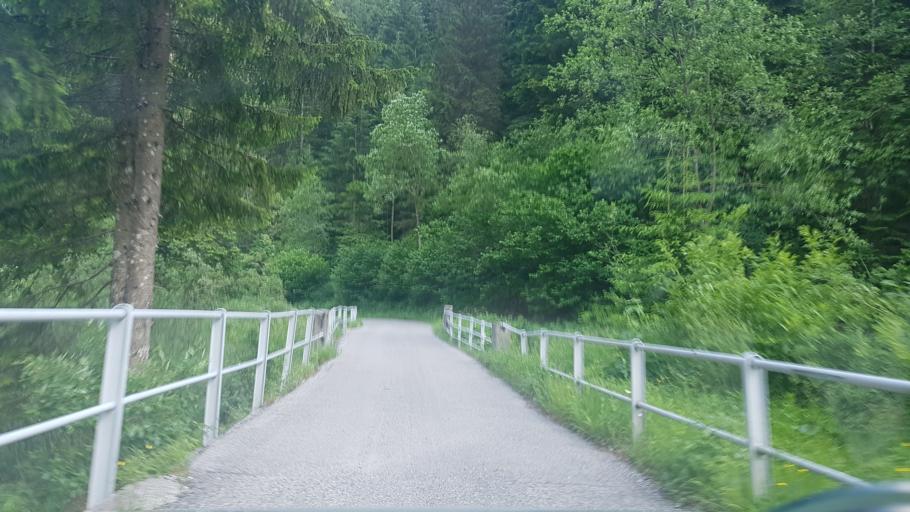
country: IT
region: Friuli Venezia Giulia
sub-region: Provincia di Udine
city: Pontebba
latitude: 46.5254
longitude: 13.2266
